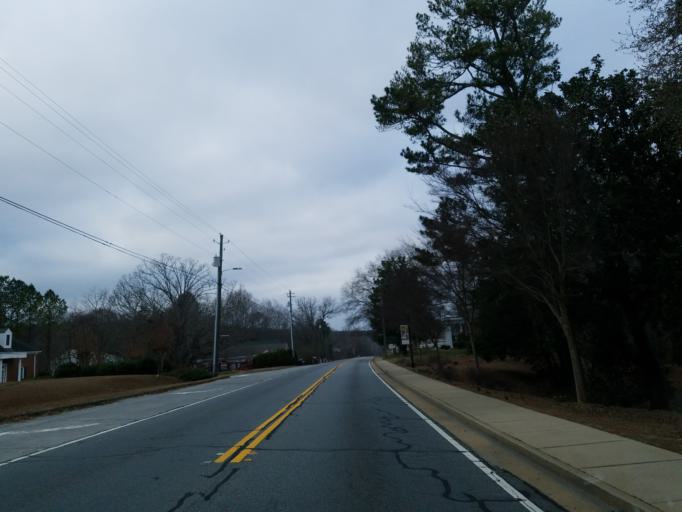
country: US
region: Georgia
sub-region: Cherokee County
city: Canton
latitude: 34.3187
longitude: -84.5555
